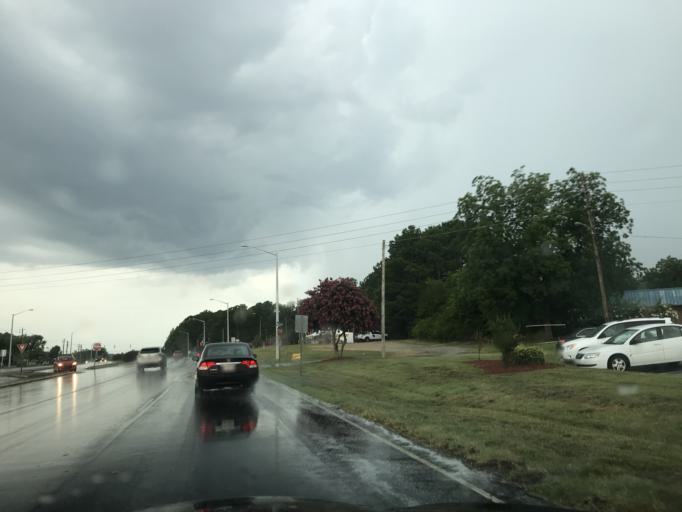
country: US
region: North Carolina
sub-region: Johnston County
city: Clayton
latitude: 35.6429
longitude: -78.4529
